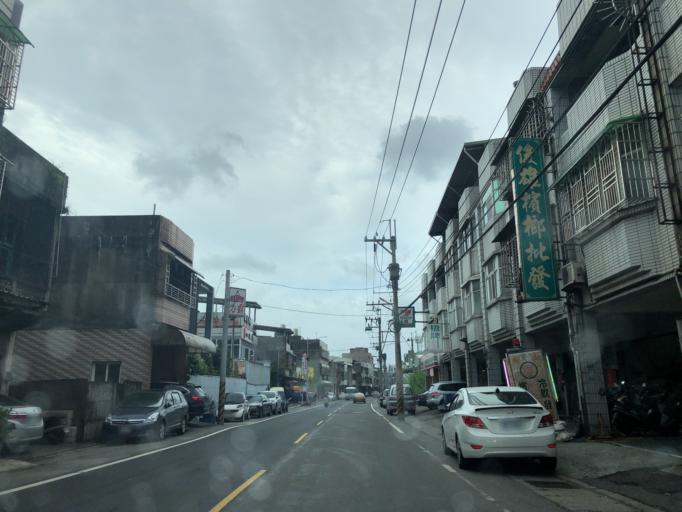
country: TW
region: Taiwan
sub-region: Taoyuan
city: Taoyuan
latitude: 24.9369
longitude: 121.3304
